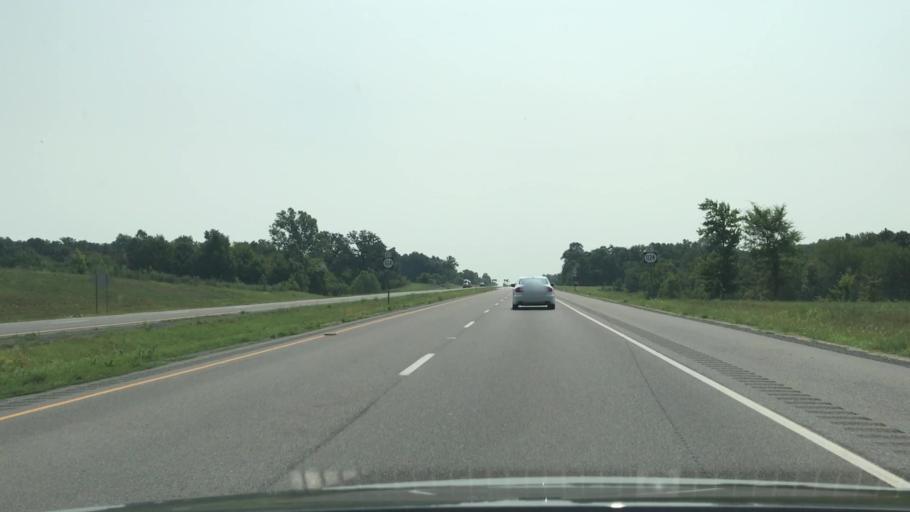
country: US
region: Kentucky
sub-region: Graves County
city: Mayfield
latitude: 36.6670
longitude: -88.4909
